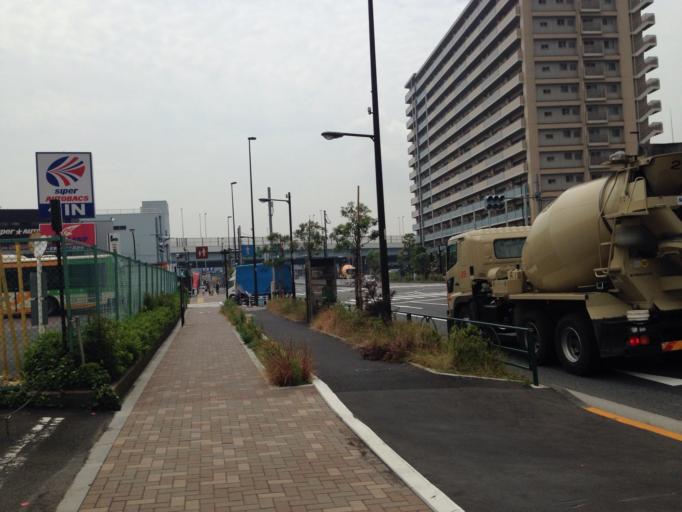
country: JP
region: Tokyo
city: Urayasu
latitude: 35.6427
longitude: 139.8025
